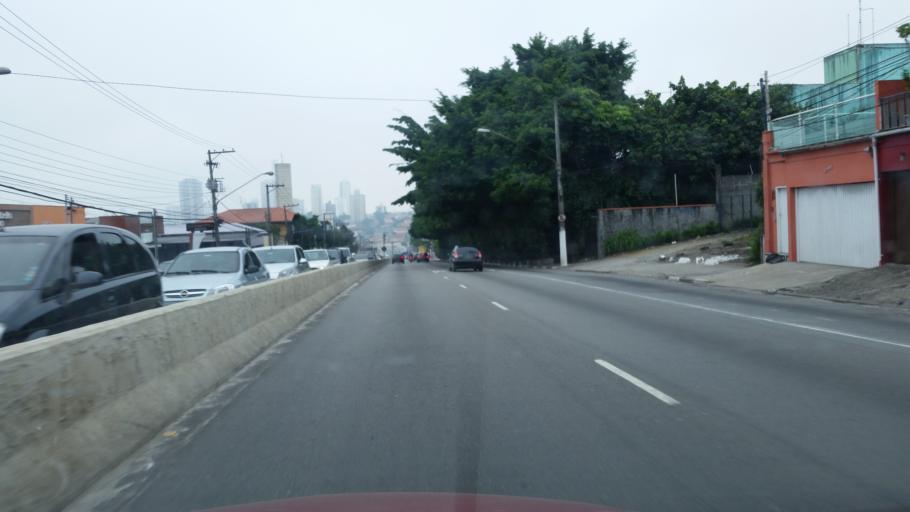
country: BR
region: Sao Paulo
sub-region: Diadema
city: Diadema
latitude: -23.6500
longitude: -46.6773
